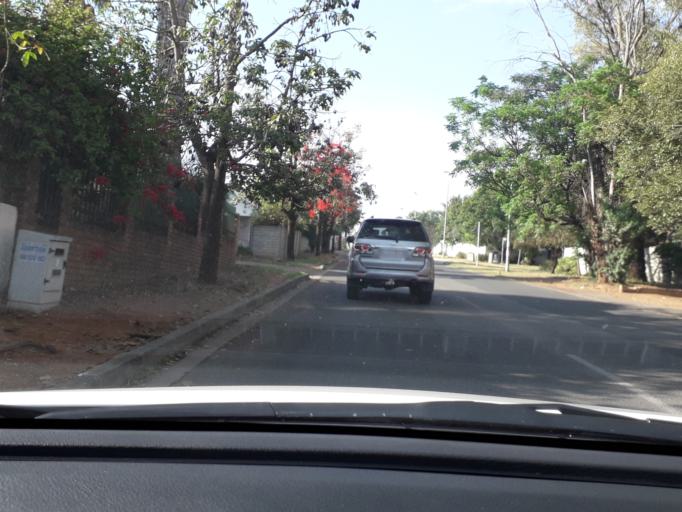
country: ZA
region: Gauteng
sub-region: City of Johannesburg Metropolitan Municipality
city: Roodepoort
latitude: -26.0764
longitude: 27.9455
